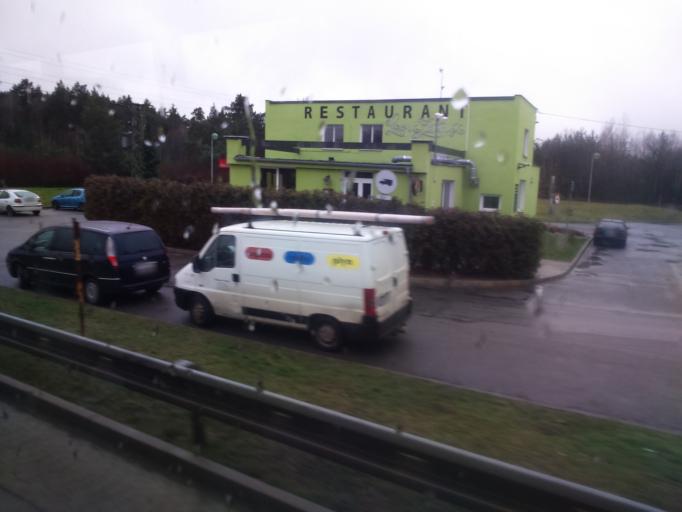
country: CZ
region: Plzensky
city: Vejprnice
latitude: 49.7177
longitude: 13.2960
